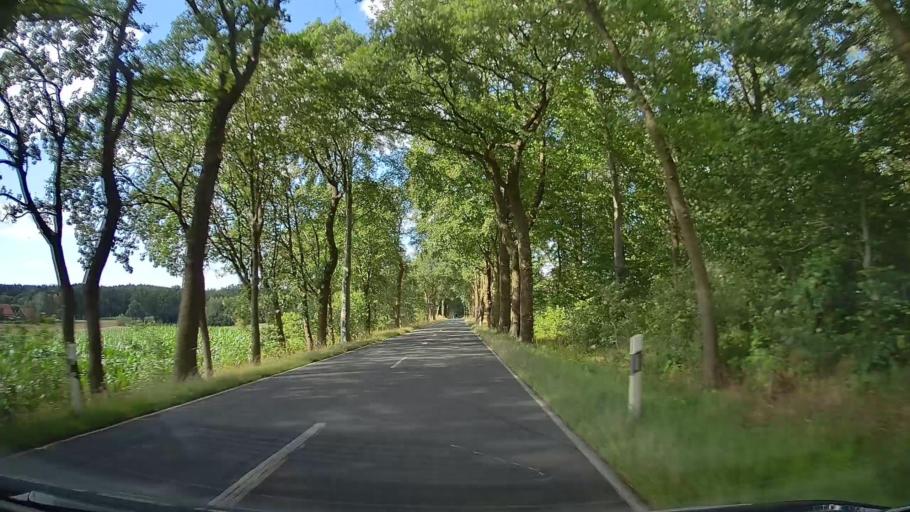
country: DE
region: Lower Saxony
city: Bippen
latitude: 52.6031
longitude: 7.7425
